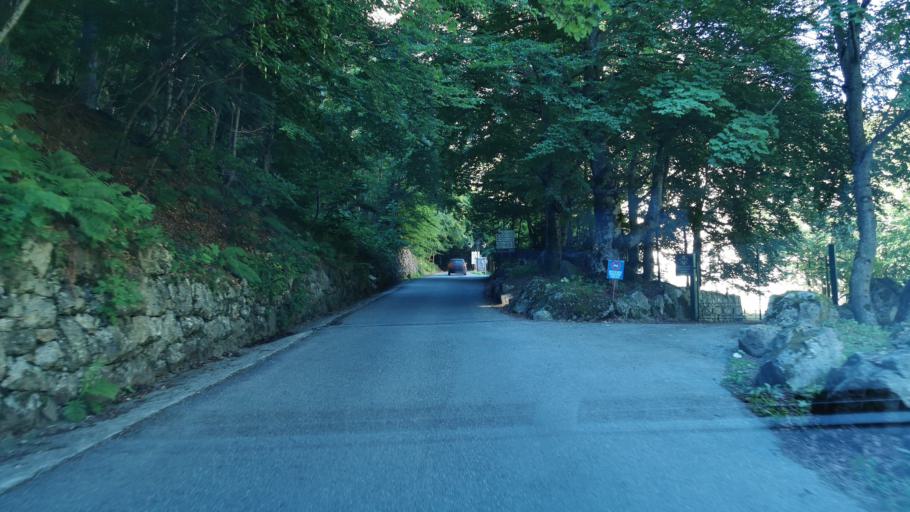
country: IT
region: Piedmont
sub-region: Provincia di Cuneo
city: Demonte
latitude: 44.2081
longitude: 7.2739
